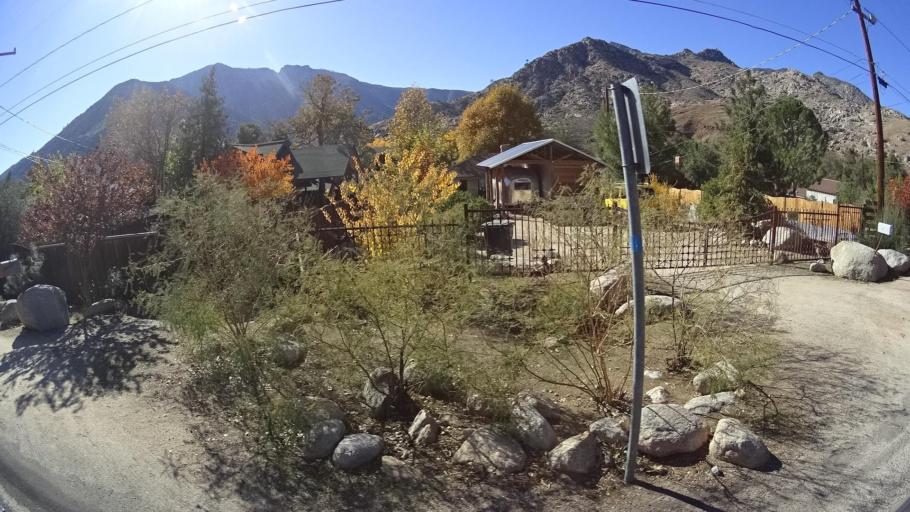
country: US
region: California
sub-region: Kern County
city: Kernville
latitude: 35.7883
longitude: -118.4474
